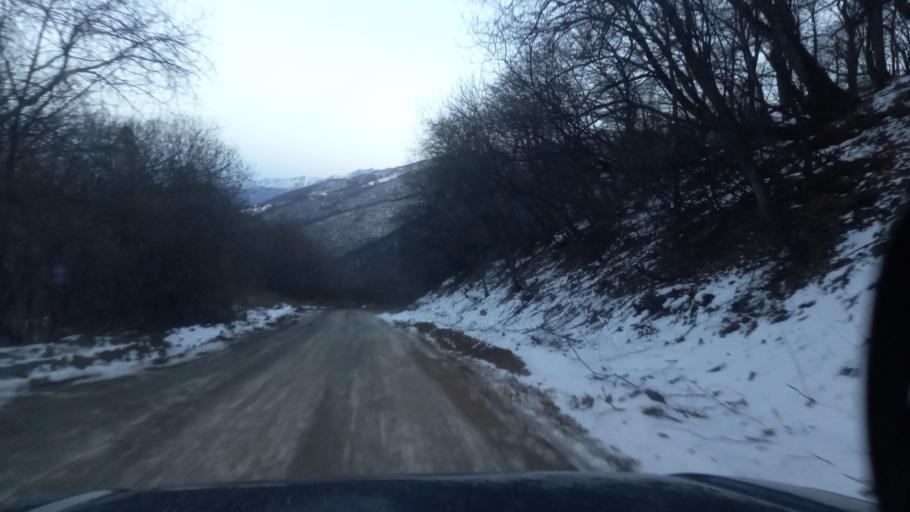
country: RU
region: Ingushetiya
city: Dzhayrakh
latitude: 42.8299
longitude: 44.5838
